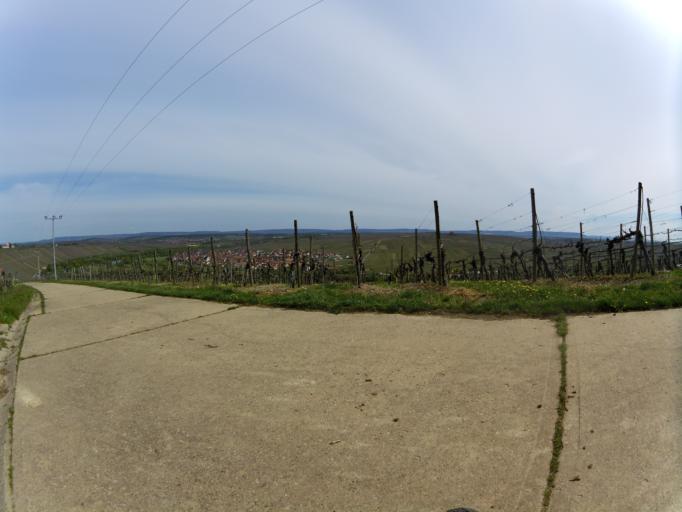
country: DE
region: Bavaria
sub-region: Regierungsbezirk Unterfranken
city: Nordheim
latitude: 49.8600
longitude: 10.1672
